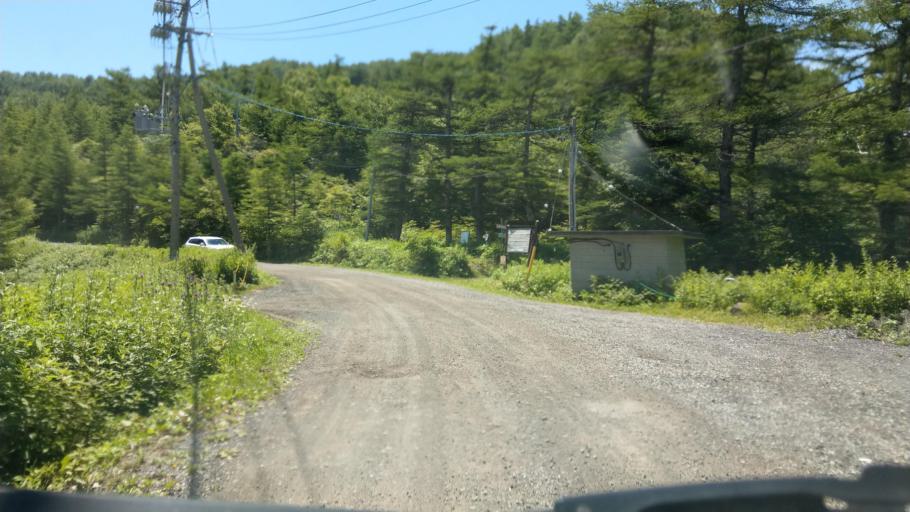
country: JP
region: Nagano
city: Komoro
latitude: 36.4091
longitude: 138.4605
